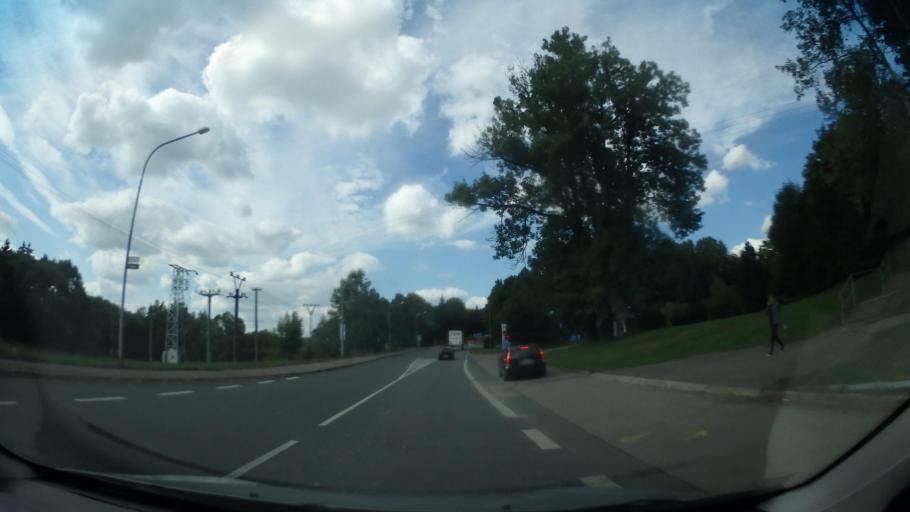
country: CZ
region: Vysocina
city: Pribyslav
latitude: 49.5715
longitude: 15.7435
